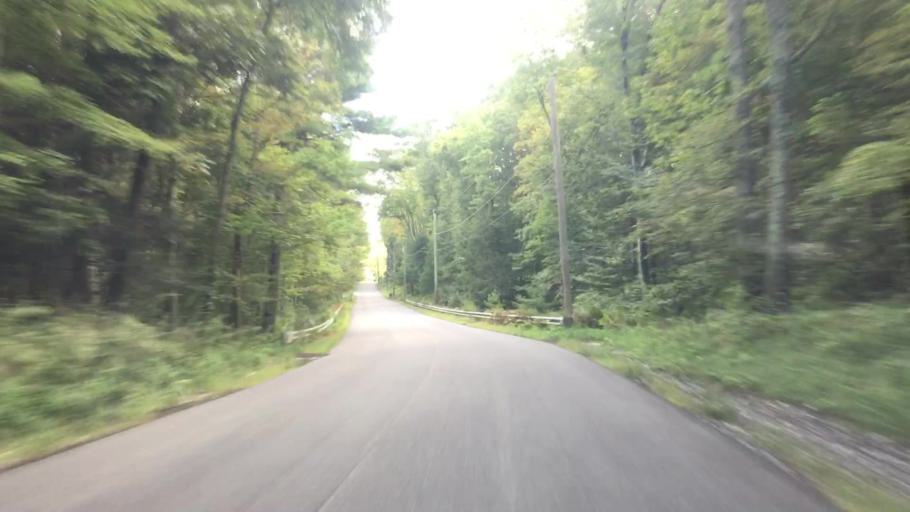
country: US
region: Connecticut
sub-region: Tolland County
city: Stafford Springs
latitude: 41.9262
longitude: -72.2489
